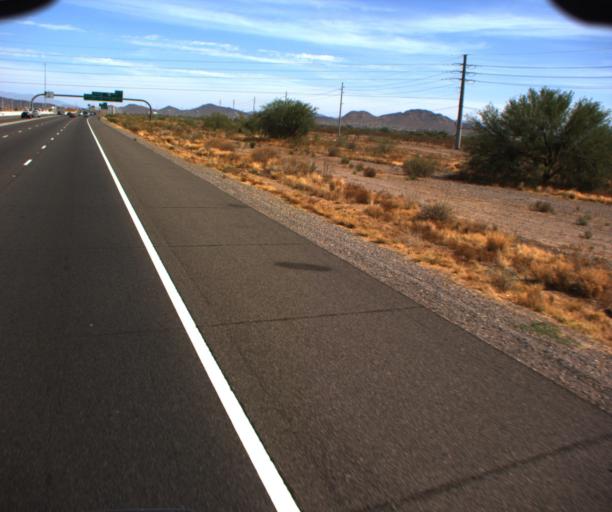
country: US
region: Arizona
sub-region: Maricopa County
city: Anthem
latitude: 33.7572
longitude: -112.1266
